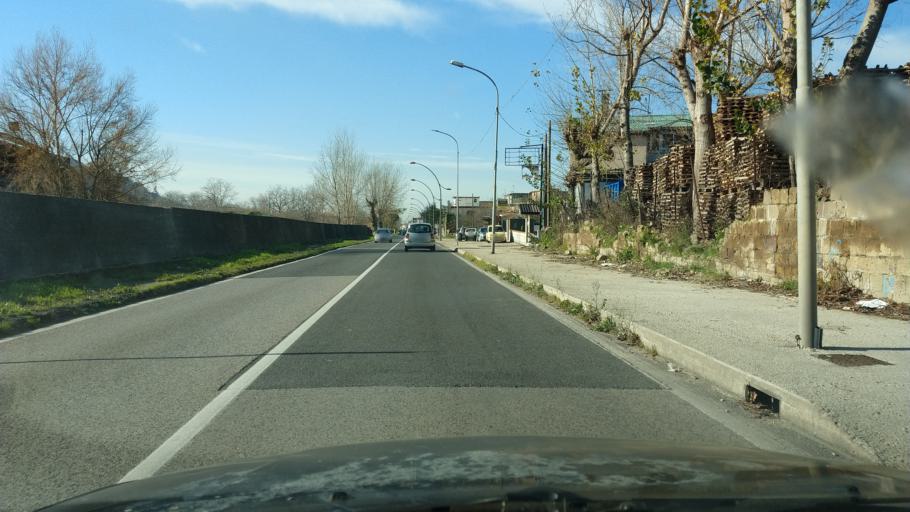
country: IT
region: Campania
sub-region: Provincia di Napoli
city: Tufino
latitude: 40.9490
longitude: 14.5822
